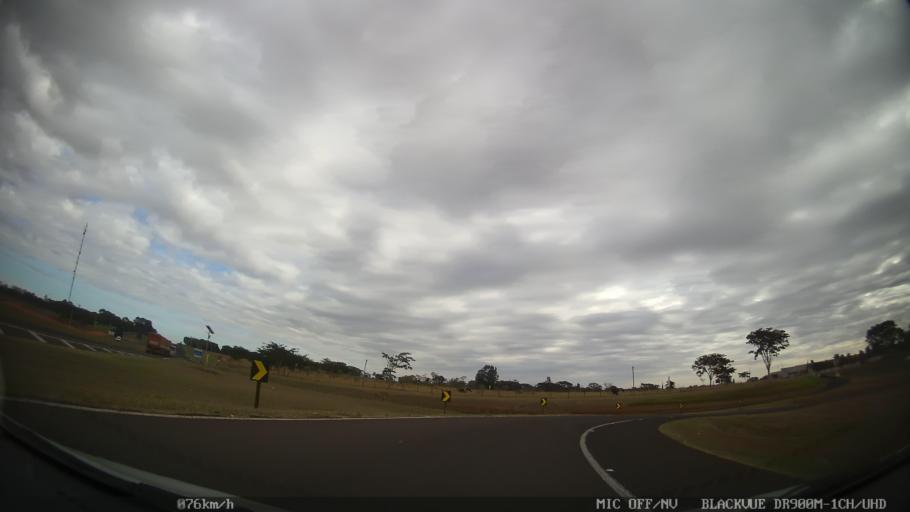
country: BR
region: Sao Paulo
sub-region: Bady Bassitt
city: Bady Bassitt
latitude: -20.8038
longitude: -49.5264
